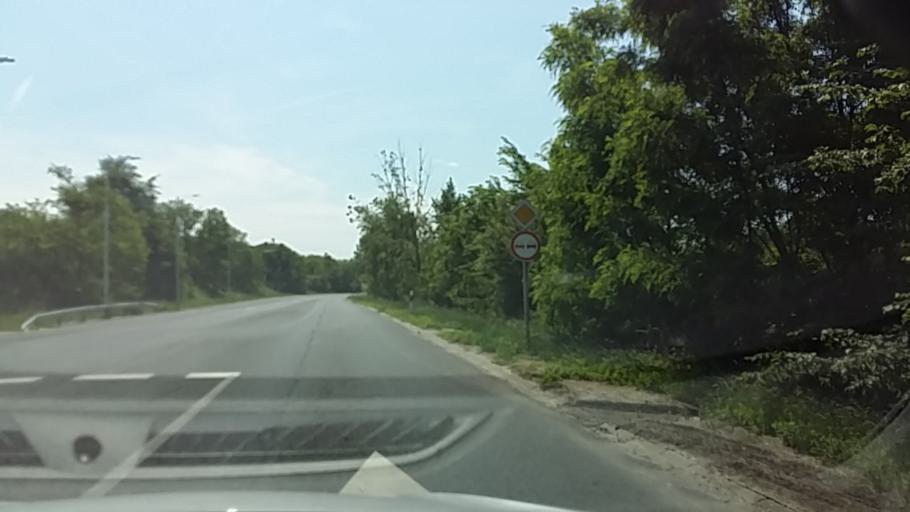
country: HU
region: Gyor-Moson-Sopron
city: Sopron
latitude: 47.6780
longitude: 16.6174
